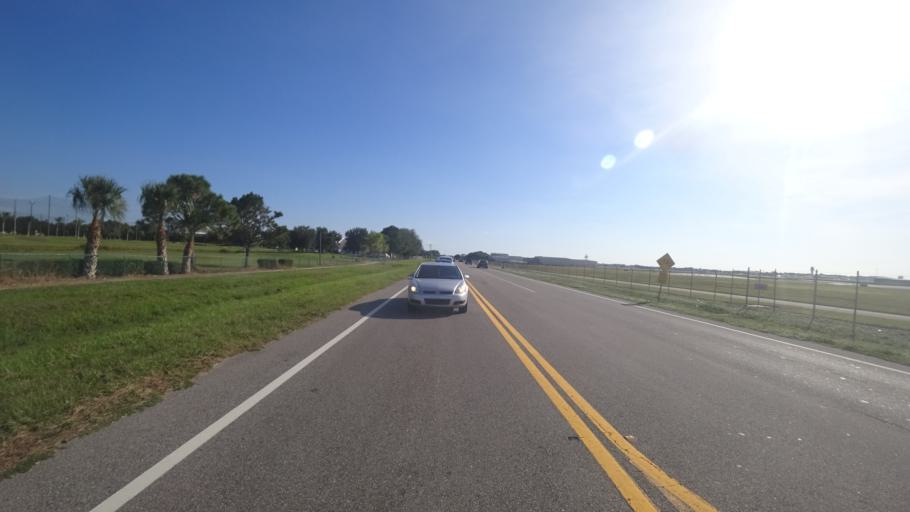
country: US
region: Florida
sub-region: Manatee County
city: Whitfield
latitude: 27.4022
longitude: -82.5468
